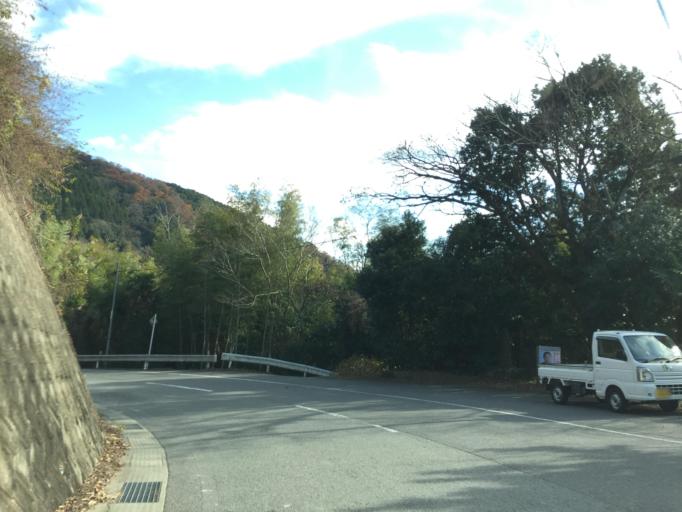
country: JP
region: Wakayama
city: Iwade
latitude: 34.1496
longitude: 135.3724
